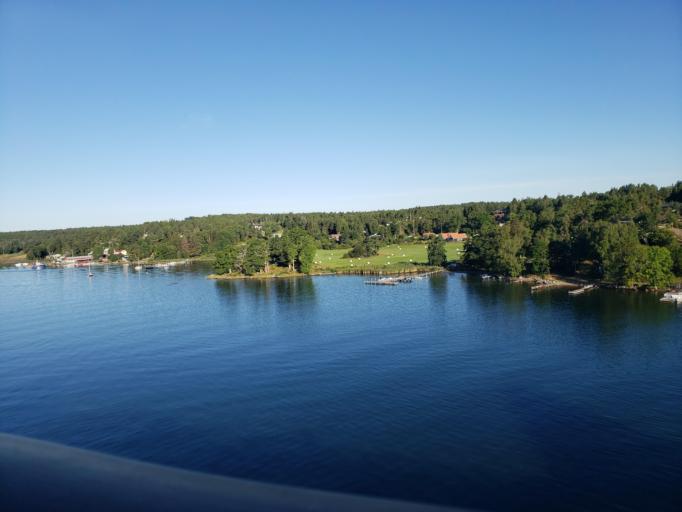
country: SE
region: Stockholm
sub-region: Vaxholms Kommun
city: Vaxholm
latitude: 59.5036
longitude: 18.4749
